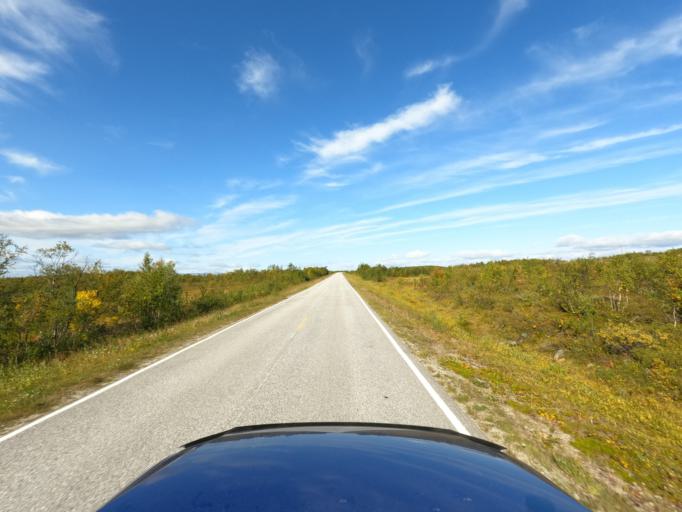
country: NO
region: Finnmark Fylke
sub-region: Karasjok
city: Karasjohka
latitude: 69.7063
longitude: 25.2479
